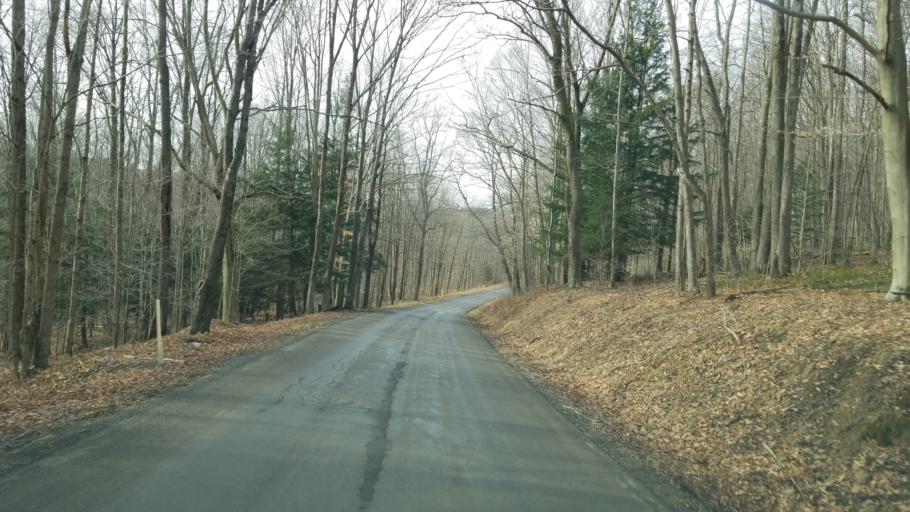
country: US
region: Pennsylvania
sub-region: Indiana County
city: Johnsonburg
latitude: 40.8329
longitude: -78.9072
